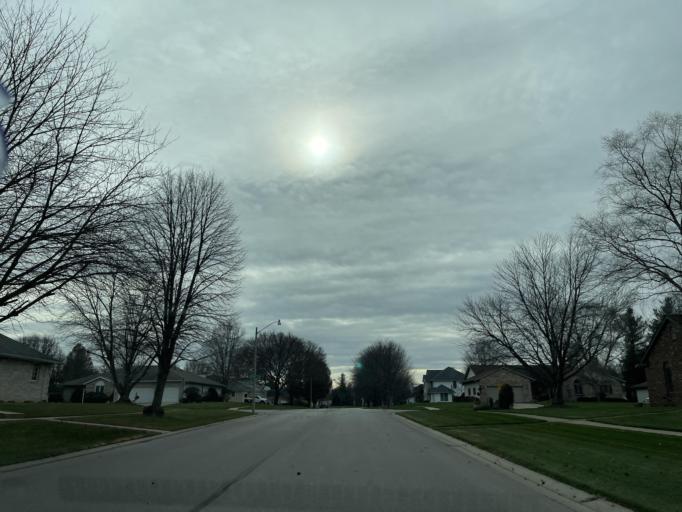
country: US
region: Illinois
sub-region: Sangamon County
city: Leland Grove
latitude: 39.7845
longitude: -89.7288
